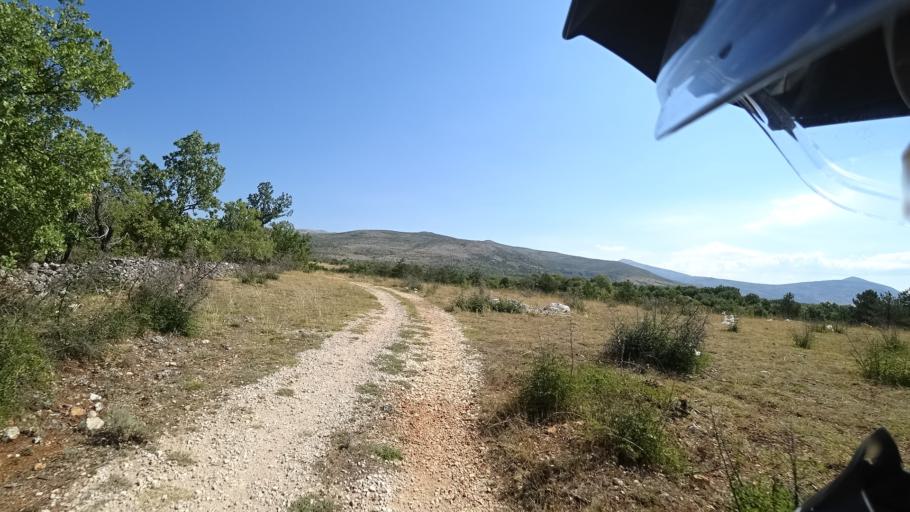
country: HR
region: Sibensko-Kniniska
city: Drnis
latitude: 43.8318
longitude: 16.2926
